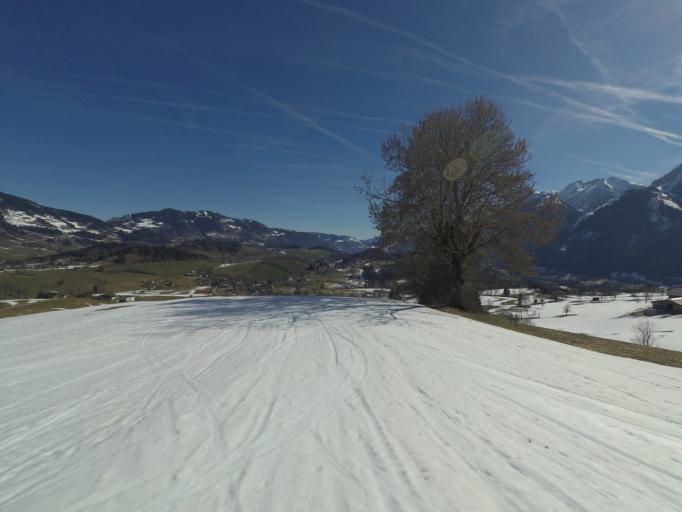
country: AT
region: Salzburg
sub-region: Politischer Bezirk Sankt Johann im Pongau
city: Goldegg
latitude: 47.3107
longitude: 13.0755
